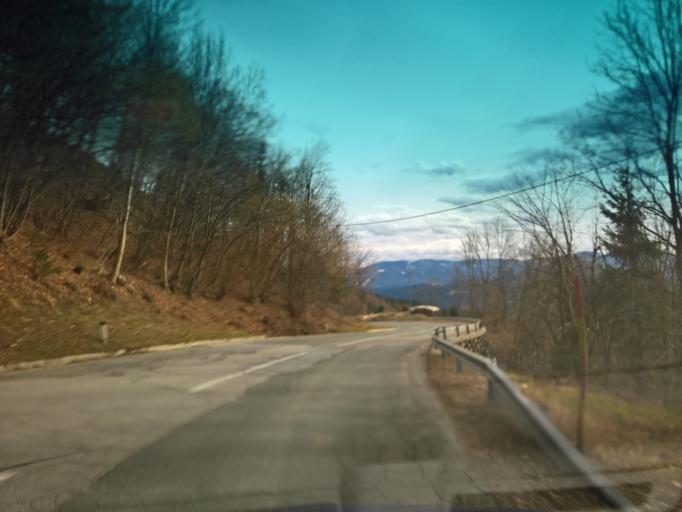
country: SI
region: Radlje ob Dravi
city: Radlje ob Dravi
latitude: 46.6394
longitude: 15.2120
